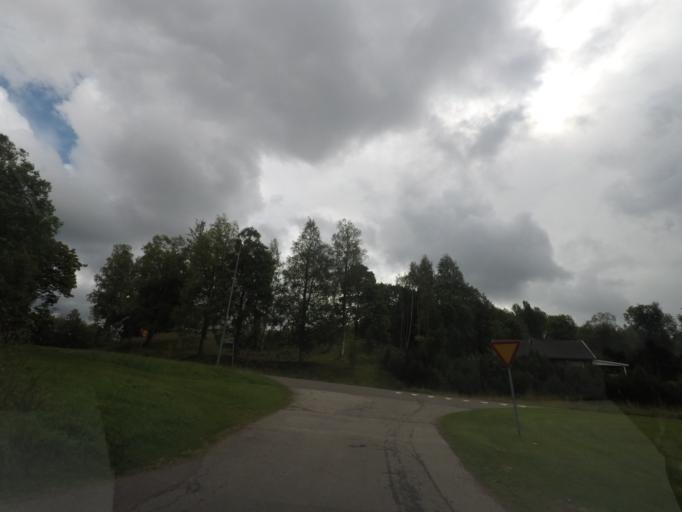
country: SE
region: Vaermland
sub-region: Filipstads Kommun
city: Lesjofors
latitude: 60.1373
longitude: 14.3930
